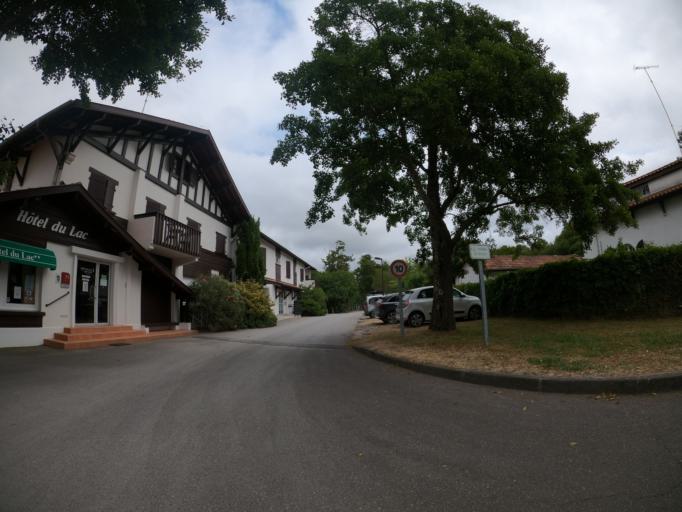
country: FR
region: Aquitaine
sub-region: Departement des Landes
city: Leon
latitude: 43.8874
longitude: -1.3161
